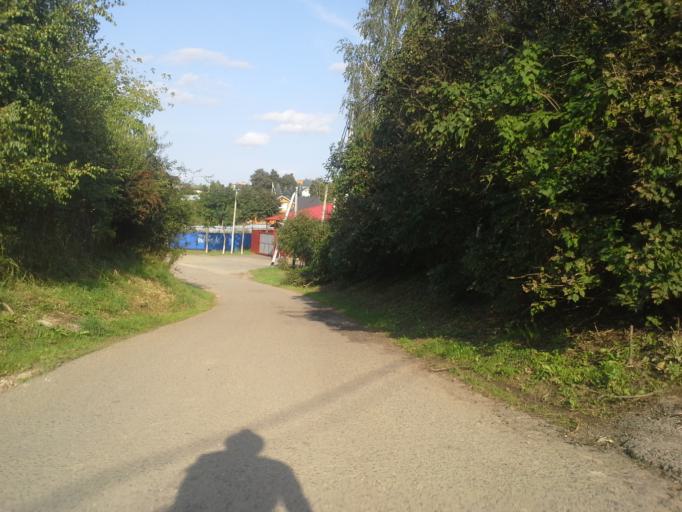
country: RU
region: Moskovskaya
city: Filimonki
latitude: 55.5394
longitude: 37.3597
